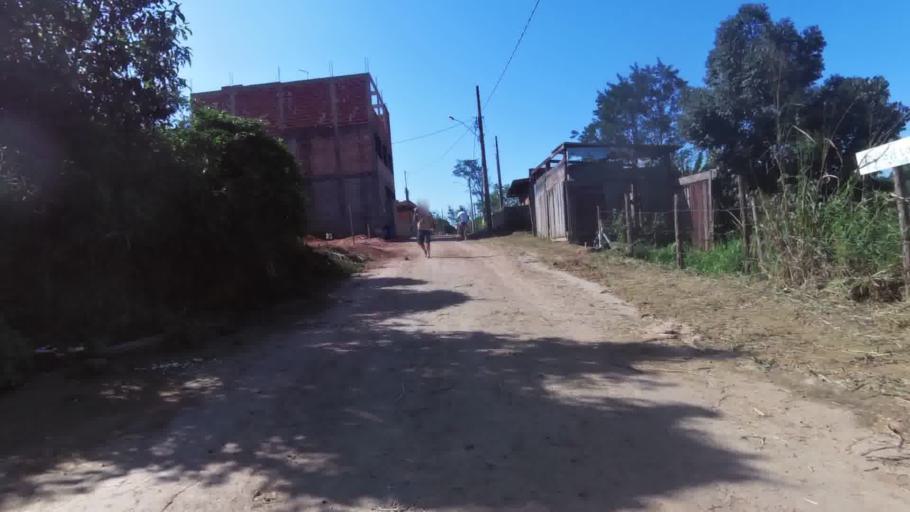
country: BR
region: Espirito Santo
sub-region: Piuma
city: Piuma
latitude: -20.8152
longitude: -40.6238
